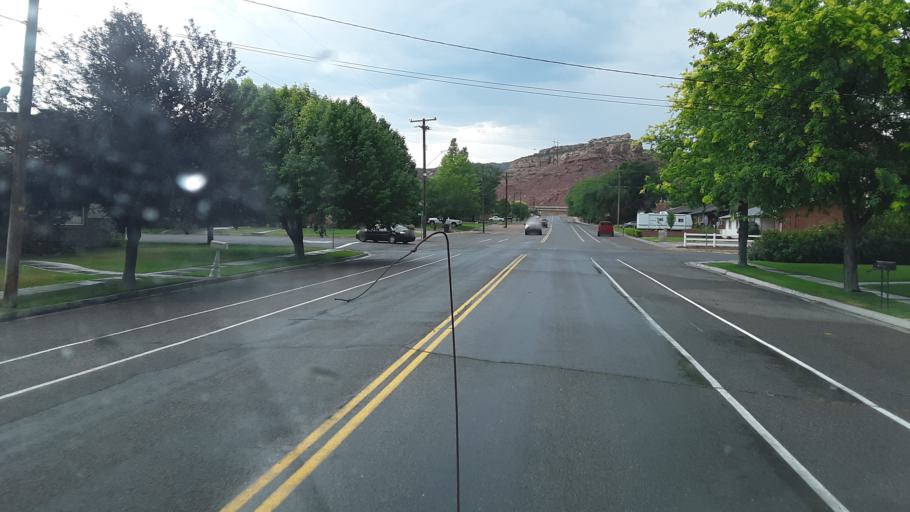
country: US
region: Utah
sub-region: Sevier County
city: Richfield
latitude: 38.7723
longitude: -112.0930
